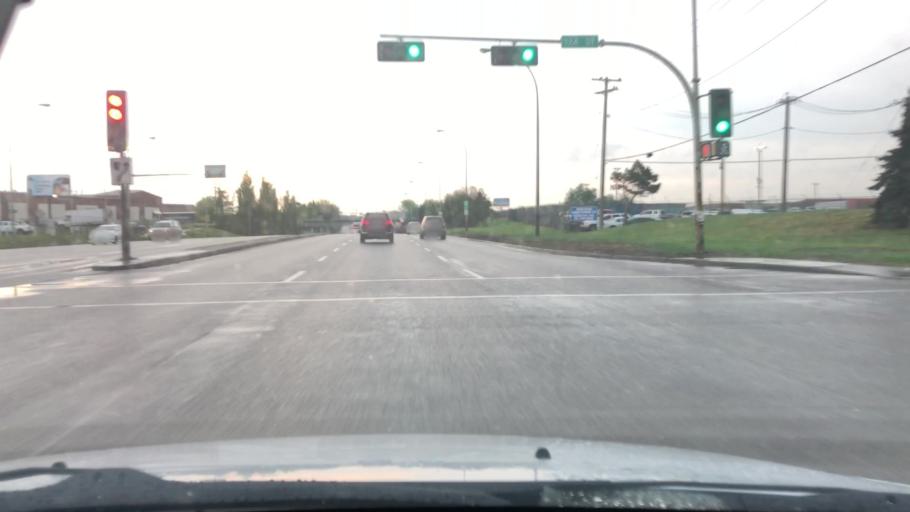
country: CA
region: Alberta
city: Edmonton
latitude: 53.5806
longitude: -113.5359
